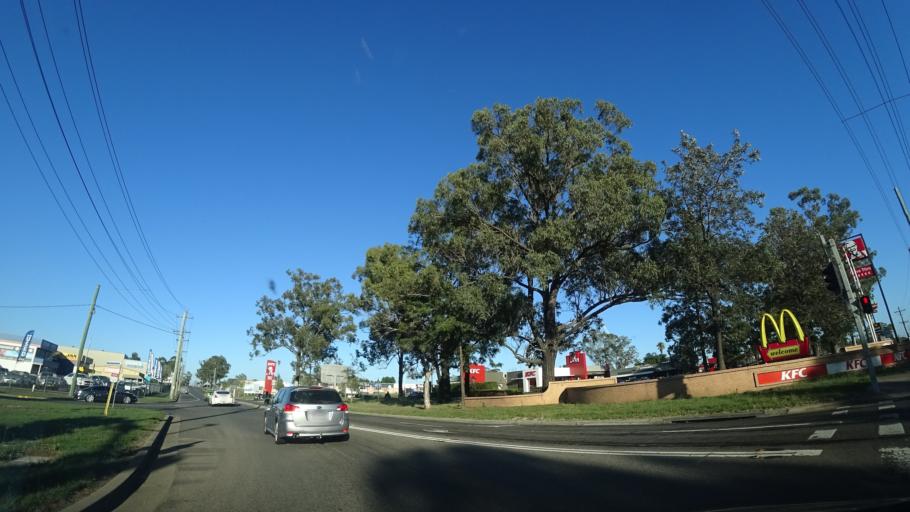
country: AU
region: New South Wales
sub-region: Hawkesbury
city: South Windsor
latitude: -33.6258
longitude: 150.8387
